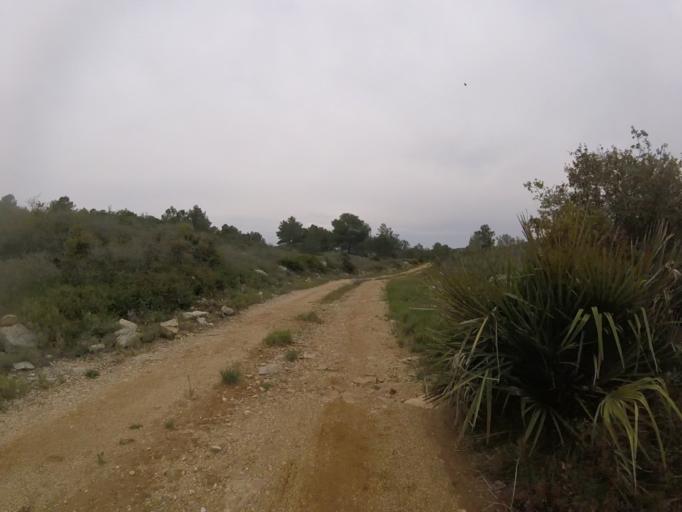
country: ES
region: Valencia
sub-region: Provincia de Castello
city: Alcala de Xivert
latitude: 40.3191
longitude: 0.2731
